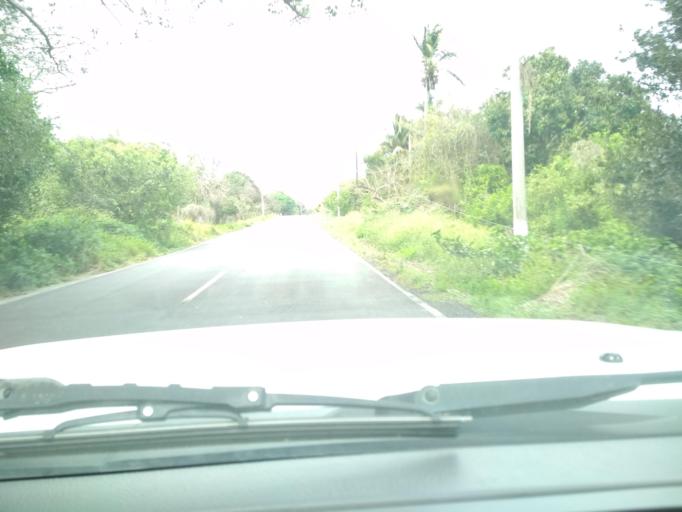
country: MX
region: Veracruz
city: Anton Lizardo
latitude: 19.0434
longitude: -95.9862
